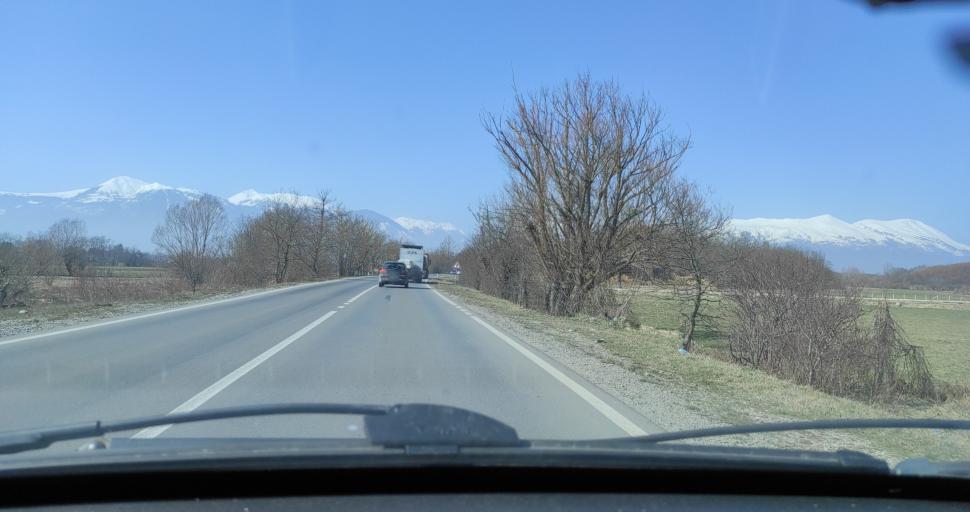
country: XK
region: Pec
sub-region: Komuna e Pejes
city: Kosuriq
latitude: 42.6368
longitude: 20.4428
